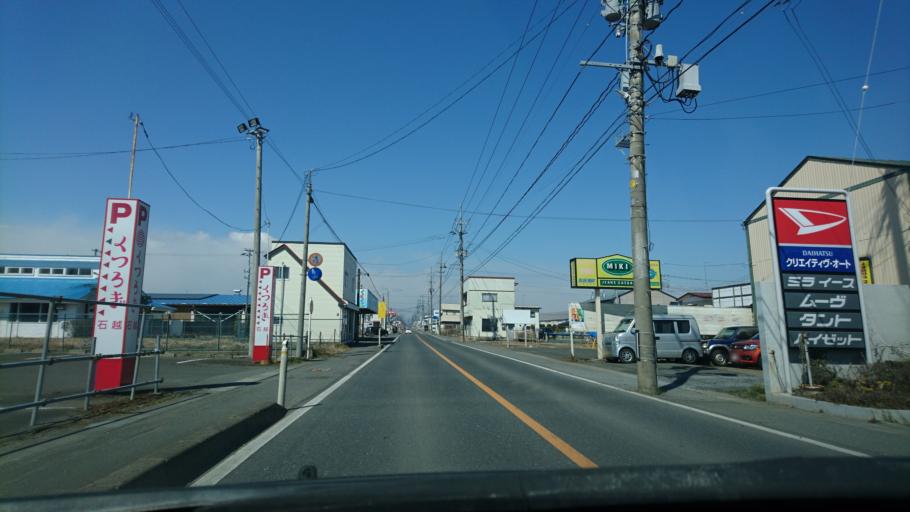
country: JP
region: Iwate
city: Ichinoseki
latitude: 38.7697
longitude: 141.1538
